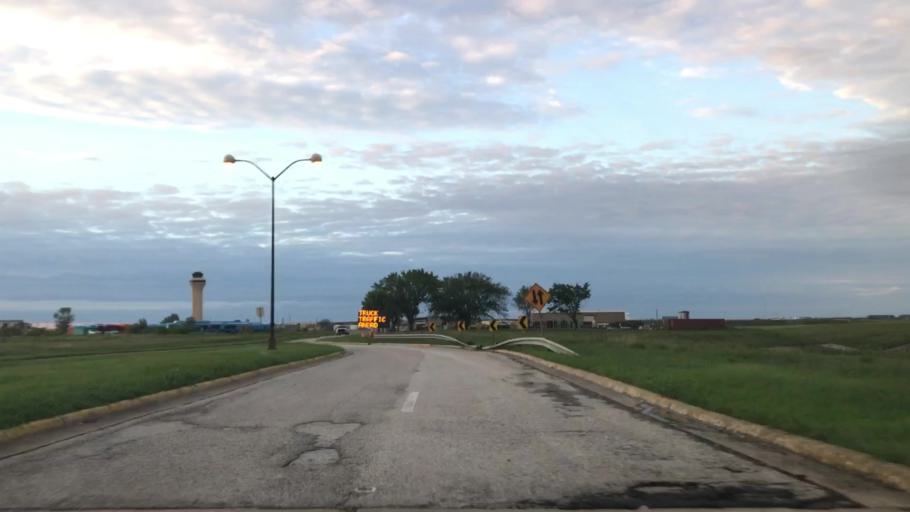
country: US
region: Texas
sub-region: Dallas County
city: Coppell
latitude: 32.8876
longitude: -97.0156
